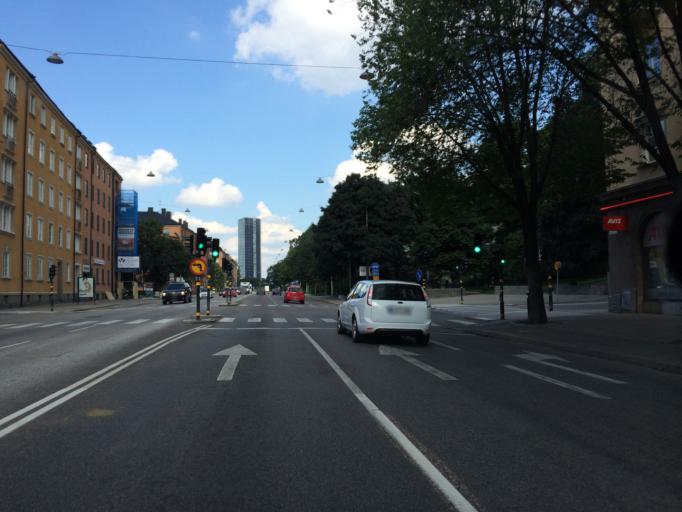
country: SE
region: Stockholm
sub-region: Stockholms Kommun
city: Stockholm
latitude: 59.3461
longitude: 18.0536
